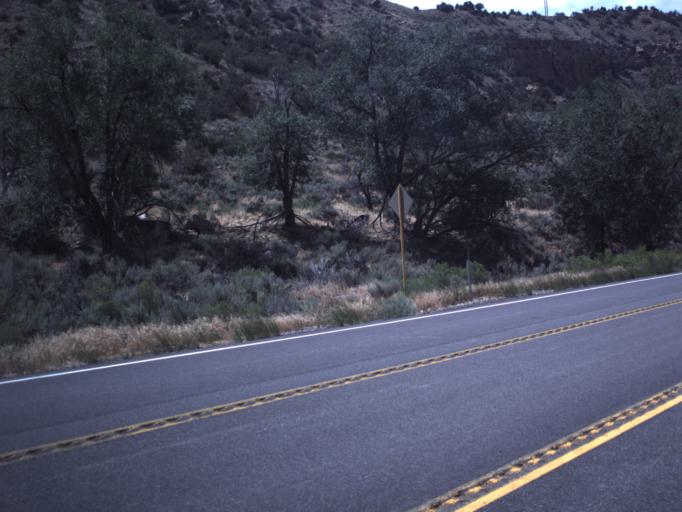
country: US
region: Utah
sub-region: Carbon County
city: Helper
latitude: 39.7280
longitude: -110.8567
